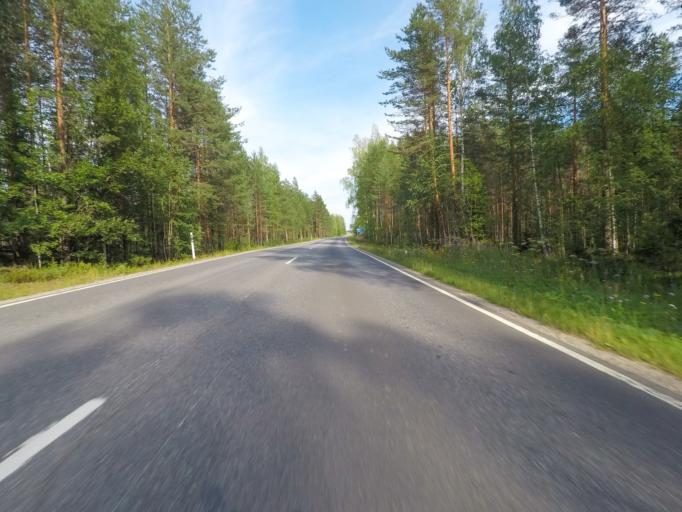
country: FI
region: Southern Savonia
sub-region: Savonlinna
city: Sulkava
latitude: 61.8066
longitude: 28.3978
